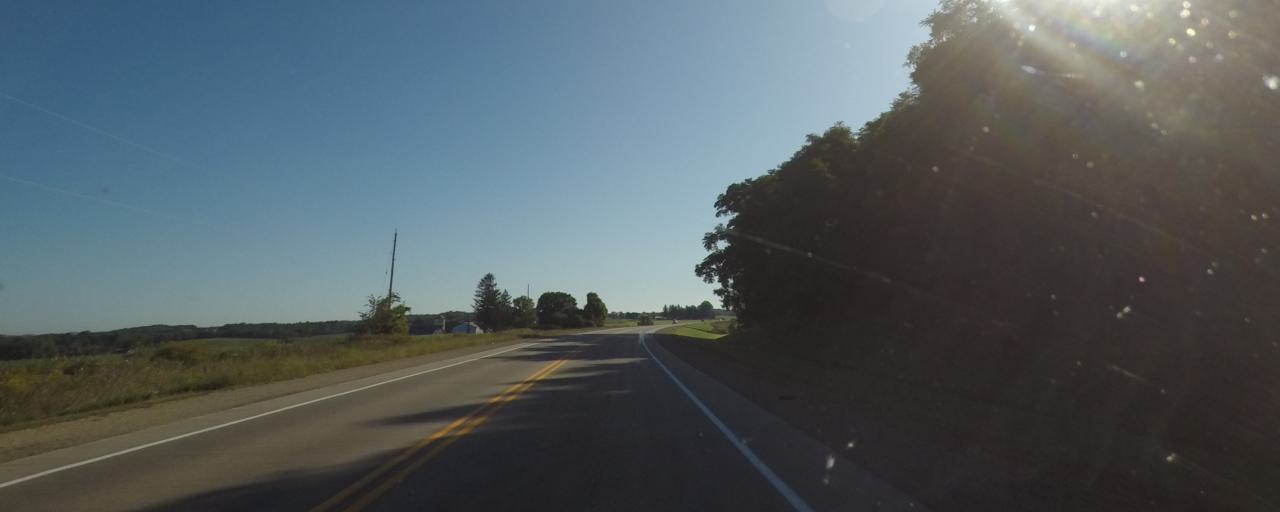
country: US
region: Wisconsin
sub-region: Dane County
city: Deerfield
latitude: 43.0343
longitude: -89.1248
